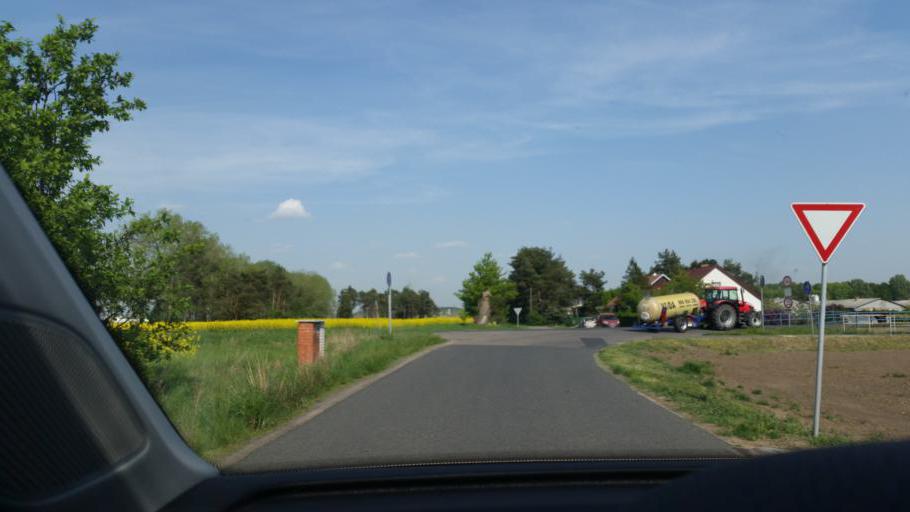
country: CZ
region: Central Bohemia
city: Veltruby
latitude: 50.0597
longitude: 15.1959
